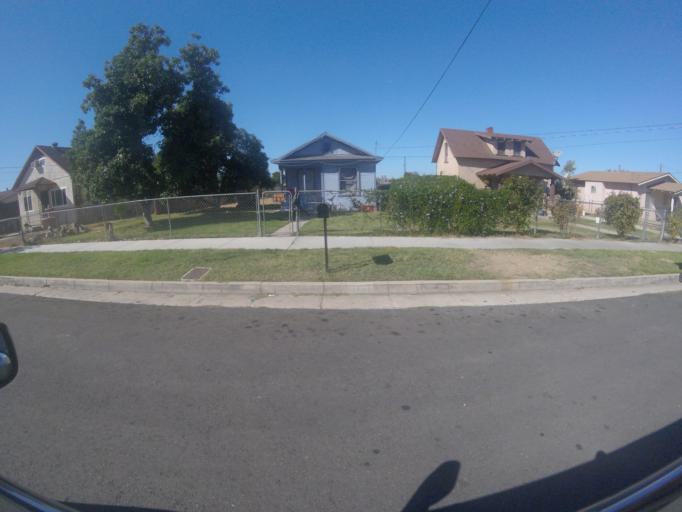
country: US
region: California
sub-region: San Bernardino County
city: Redlands
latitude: 34.0676
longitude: -117.1868
